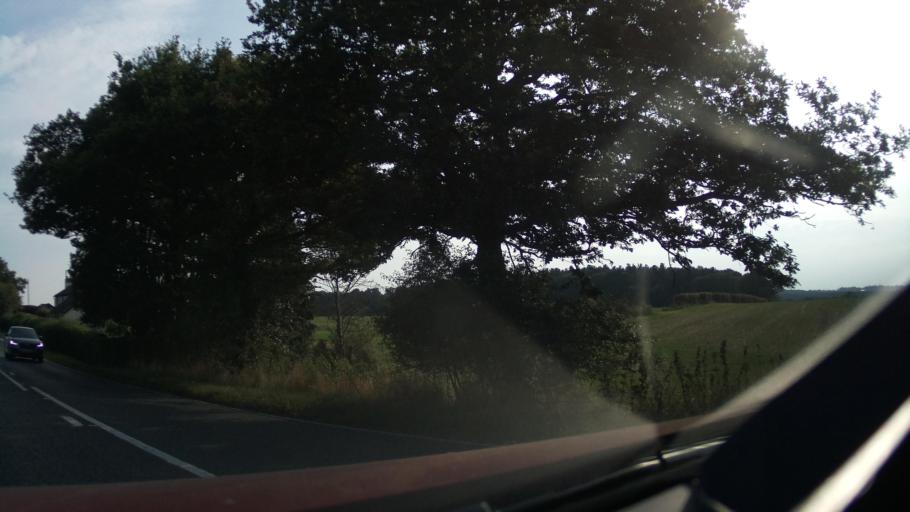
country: GB
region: England
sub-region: Warwickshire
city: Studley
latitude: 52.2549
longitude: -1.8884
